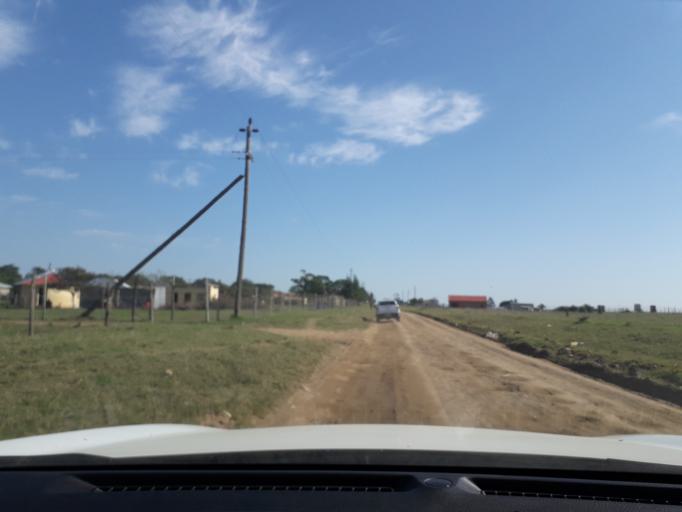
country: ZA
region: Eastern Cape
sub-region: Buffalo City Metropolitan Municipality
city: Bhisho
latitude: -32.9716
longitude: 27.3147
